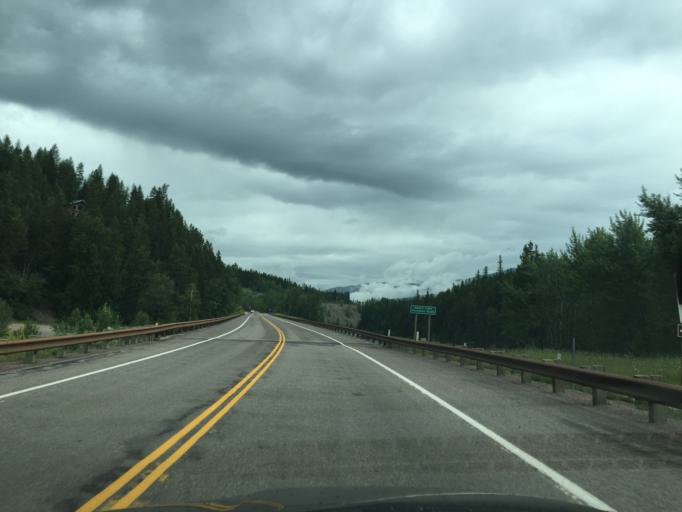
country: US
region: Montana
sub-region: Flathead County
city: Bigfork
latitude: 48.2738
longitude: -113.6040
